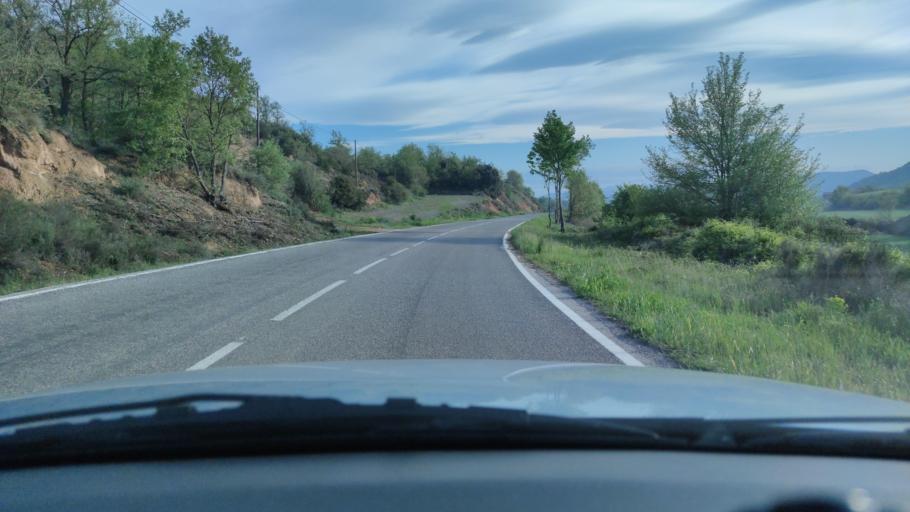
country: ES
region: Catalonia
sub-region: Provincia de Lleida
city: Ponts
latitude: 41.8827
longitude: 1.1810
